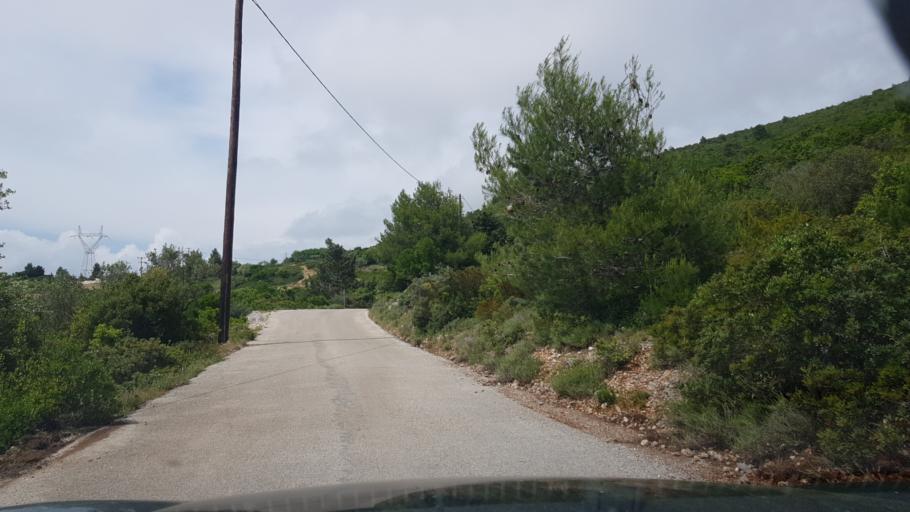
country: GR
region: Ionian Islands
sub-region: Lefkada
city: Nidri
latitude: 38.6165
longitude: 20.5655
